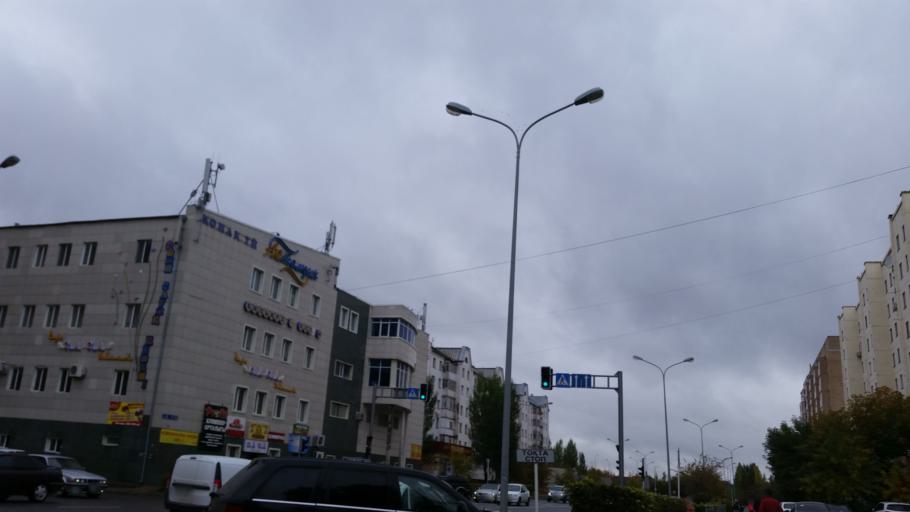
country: KZ
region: Astana Qalasy
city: Astana
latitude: 51.1518
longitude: 71.5000
